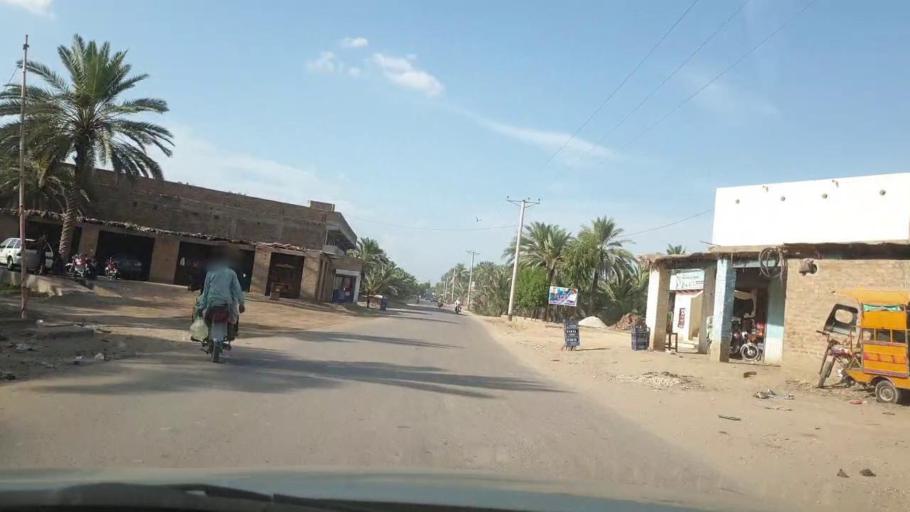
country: PK
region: Sindh
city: Sukkur
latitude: 27.6585
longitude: 68.8418
